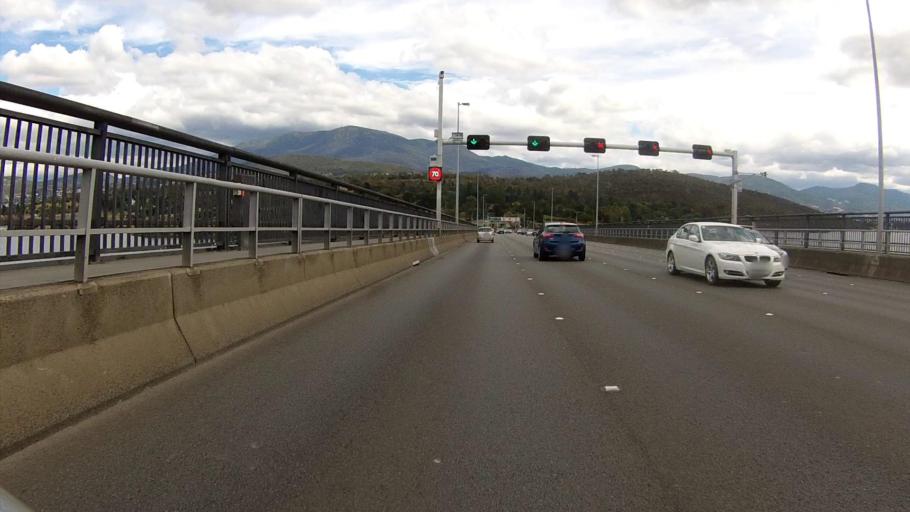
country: AU
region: Tasmania
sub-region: Hobart
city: Hobart
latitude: -42.8651
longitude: 147.3414
